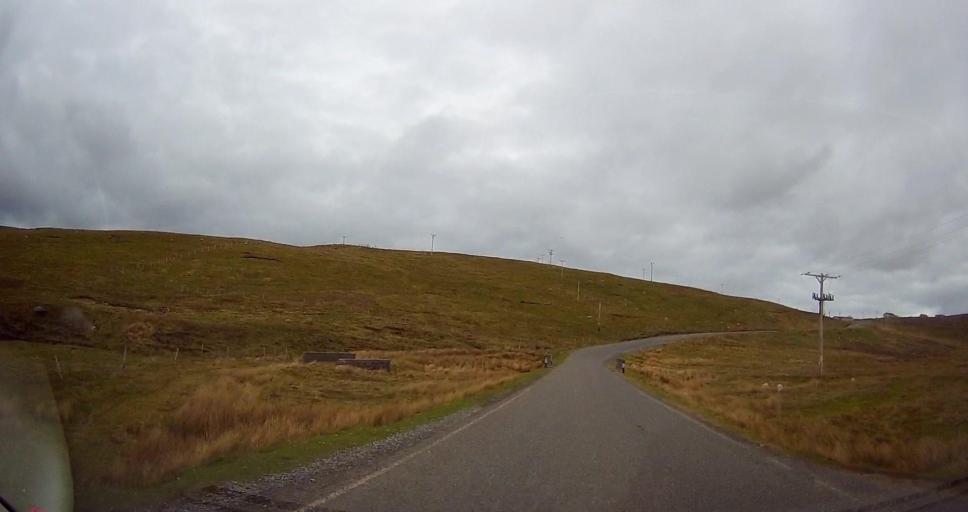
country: GB
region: Scotland
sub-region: Shetland Islands
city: Shetland
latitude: 60.6030
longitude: -1.0835
